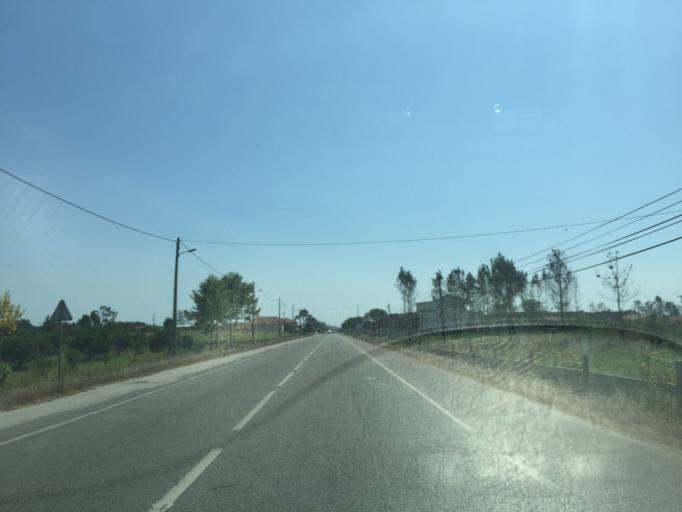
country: PT
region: Coimbra
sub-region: Mira
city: Mira
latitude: 40.3271
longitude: -8.7516
